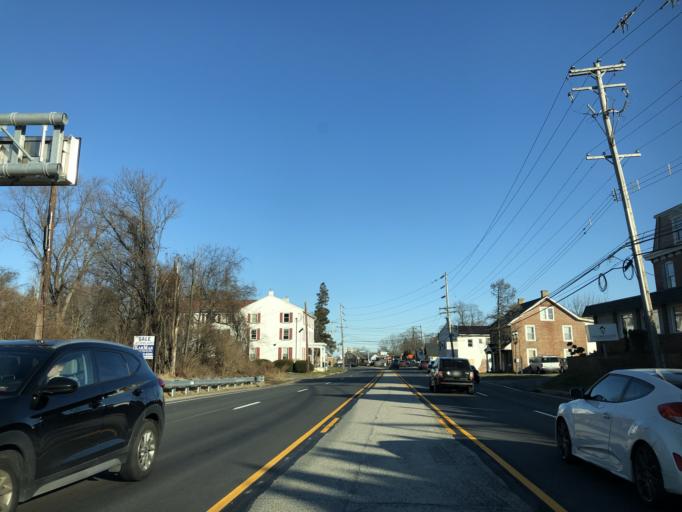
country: US
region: Pennsylvania
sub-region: Delaware County
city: Chester Heights
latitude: 39.8861
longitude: -75.5247
